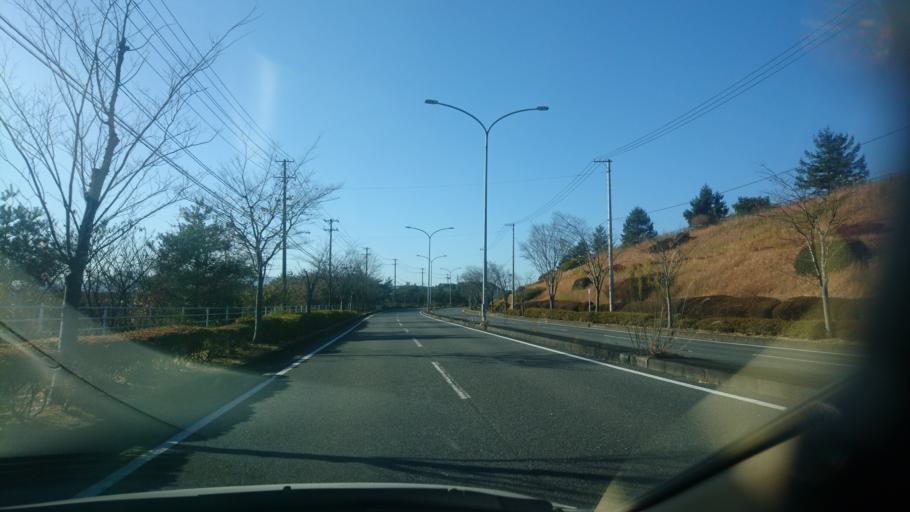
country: JP
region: Miyagi
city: Tomiya
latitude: 38.4585
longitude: 140.9251
